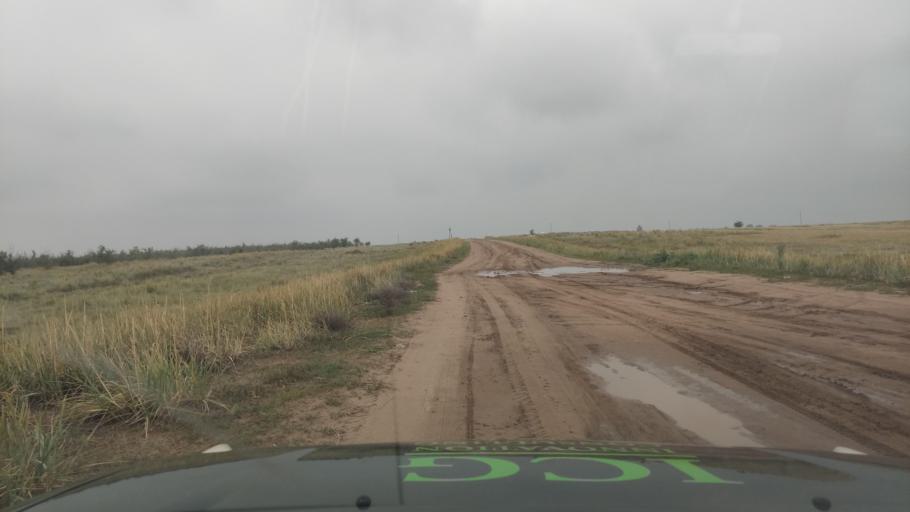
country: KZ
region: Pavlodar
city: Aksu
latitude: 52.0594
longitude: 77.1527
